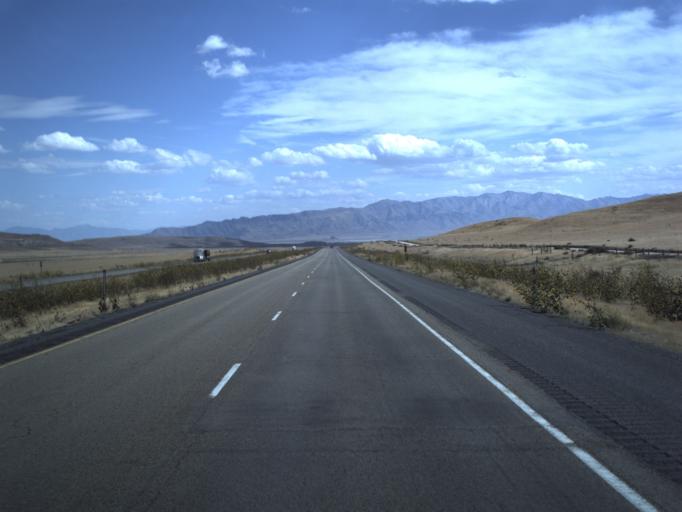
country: US
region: Utah
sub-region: Tooele County
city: Grantsville
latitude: 40.8144
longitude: -112.8760
